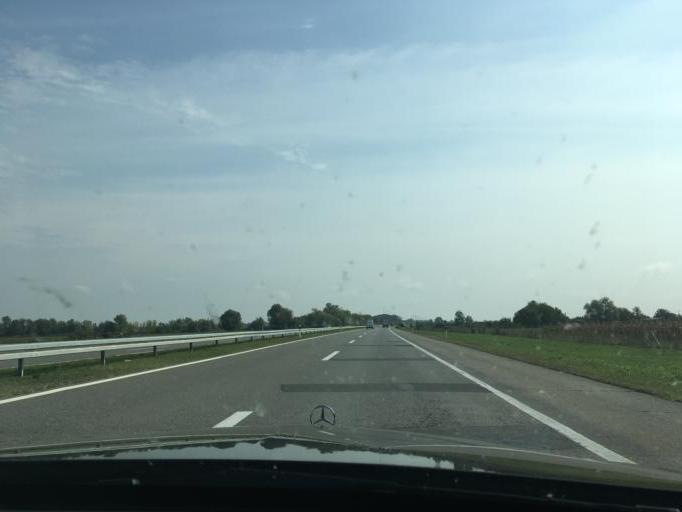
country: HR
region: Vukovarsko-Srijemska
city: Stitar
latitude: 45.1105
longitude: 18.6711
